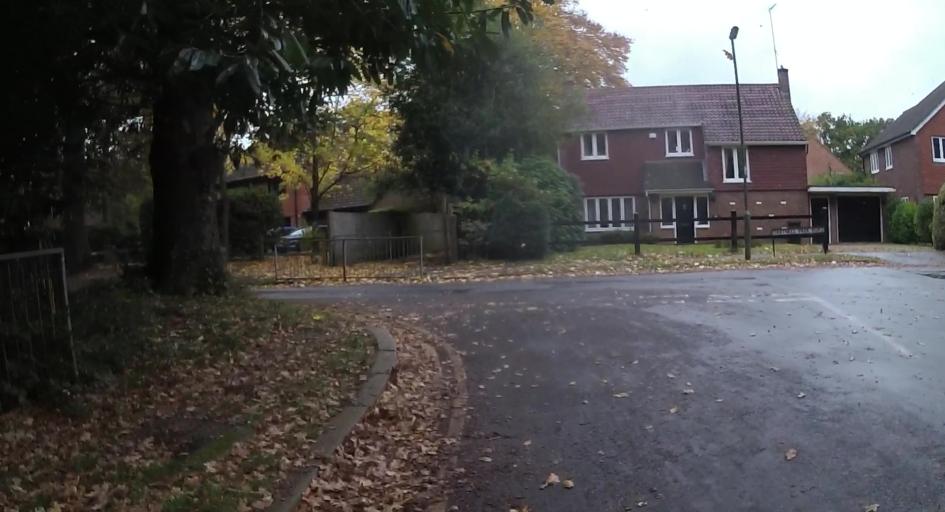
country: GB
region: England
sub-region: Surrey
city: West Byfleet
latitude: 51.3414
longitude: -0.4952
